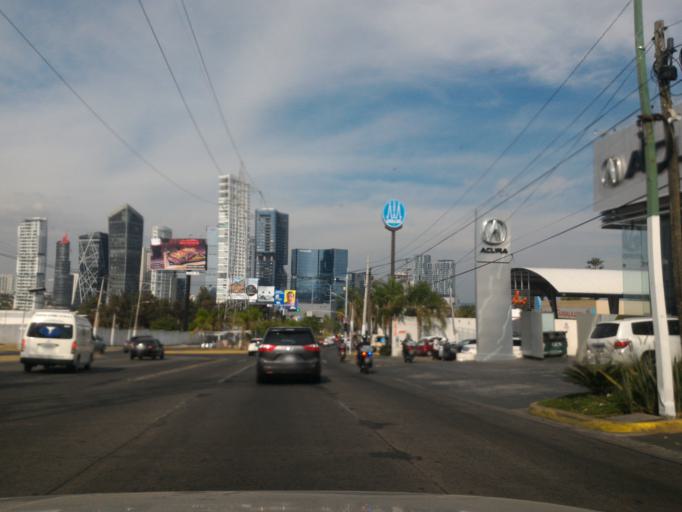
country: MX
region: Jalisco
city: Zapopan2
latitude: 20.7012
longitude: -103.4154
